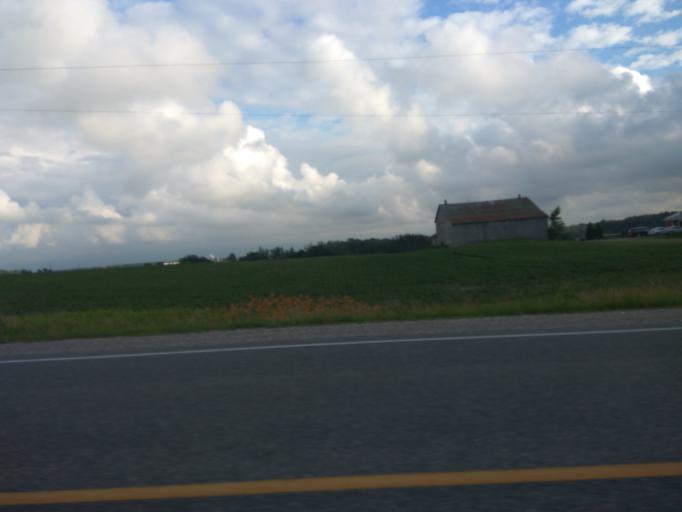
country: CA
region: Ontario
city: Stratford
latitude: 43.3691
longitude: -80.7895
